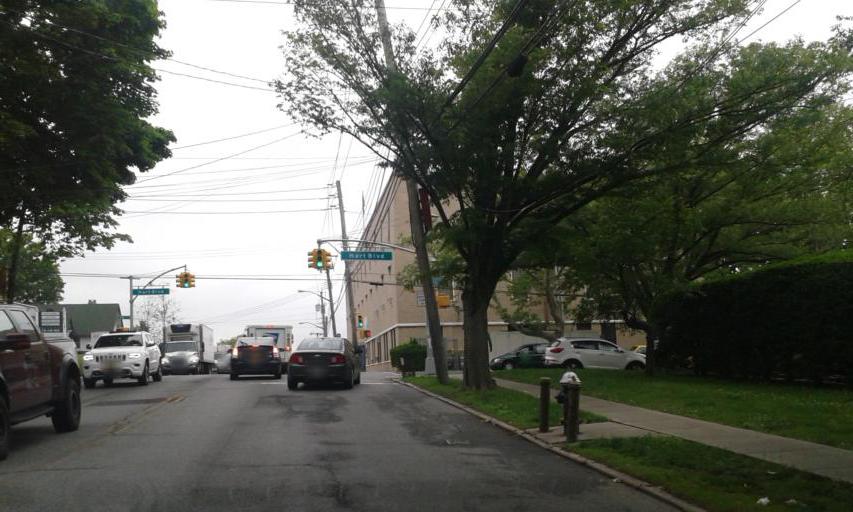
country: US
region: New Jersey
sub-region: Hudson County
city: Bayonne
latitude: 40.6314
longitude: -74.0997
